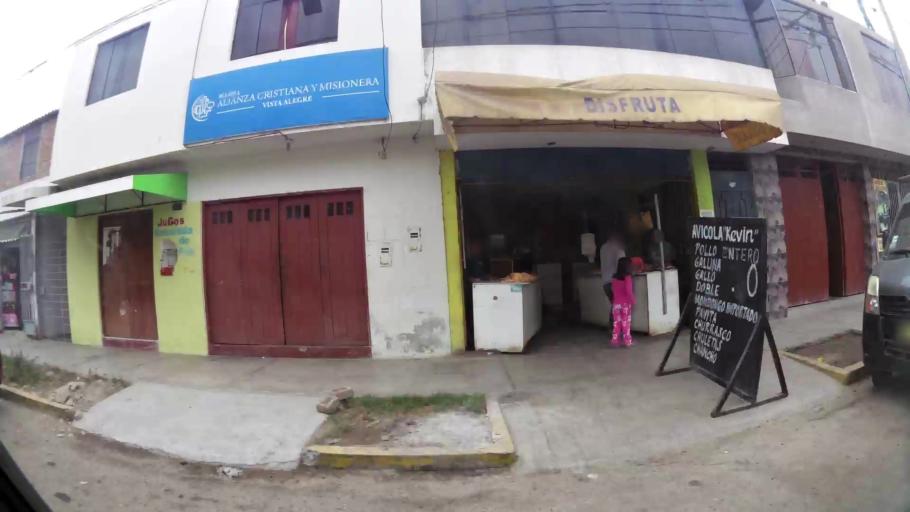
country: PE
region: La Libertad
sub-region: Provincia de Trujillo
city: Buenos Aires
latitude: -8.1363
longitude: -79.0445
